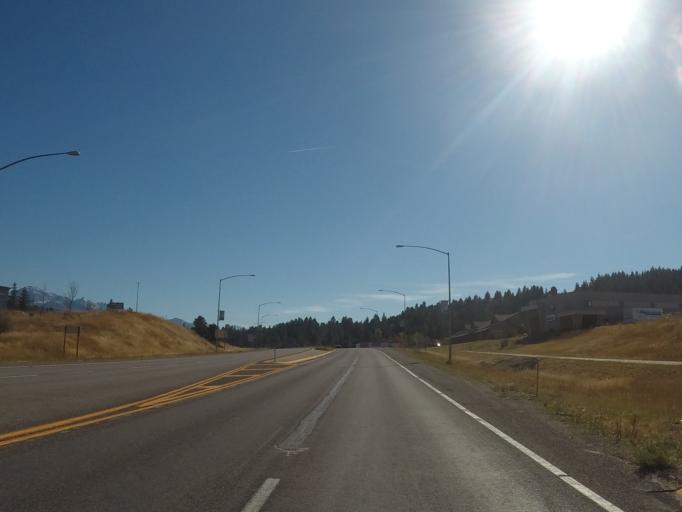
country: US
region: Montana
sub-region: Lake County
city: Polson
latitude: 47.6848
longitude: -114.1234
